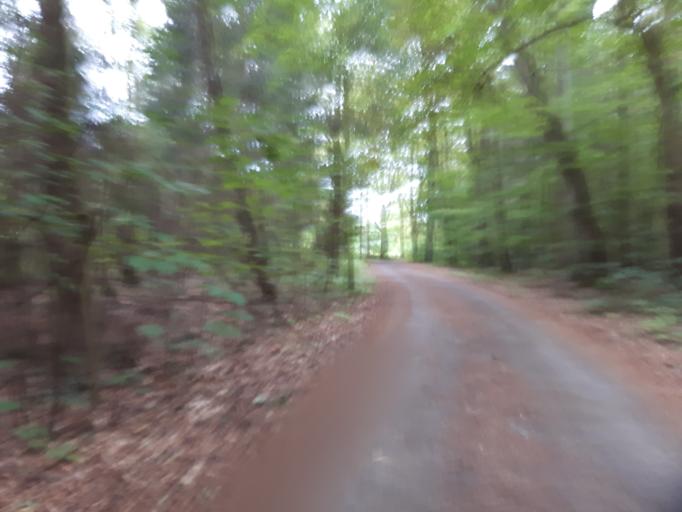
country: DE
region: Lower Saxony
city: Vierhofen
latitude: 53.2653
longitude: 10.1864
